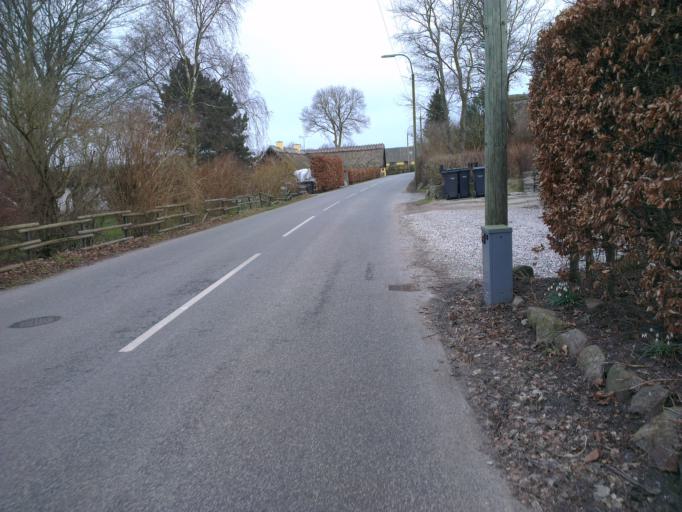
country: DK
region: Capital Region
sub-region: Frederikssund Kommune
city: Skibby
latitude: 55.7615
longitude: 11.8863
